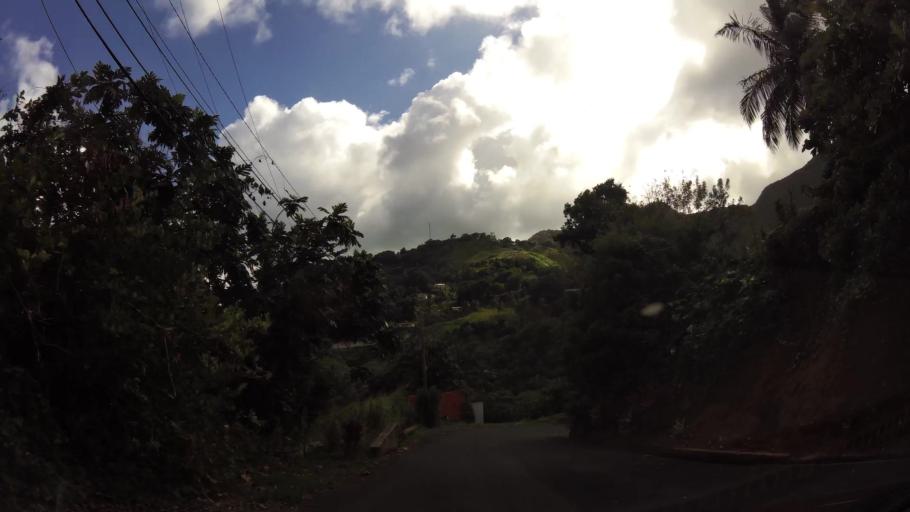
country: DM
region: Saint Andrew
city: Calibishie
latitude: 15.6131
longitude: -61.4039
